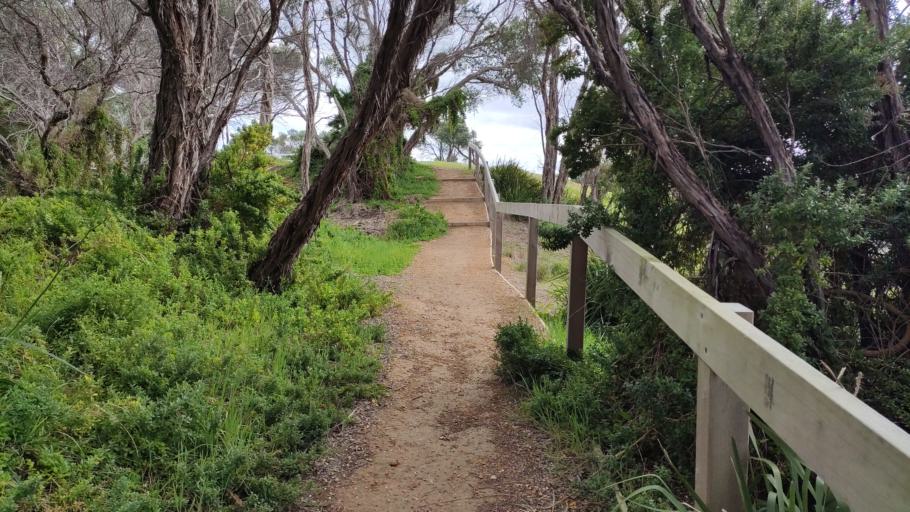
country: AU
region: Victoria
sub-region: Moyne
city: Port Fairy
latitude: -38.3888
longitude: 142.2435
